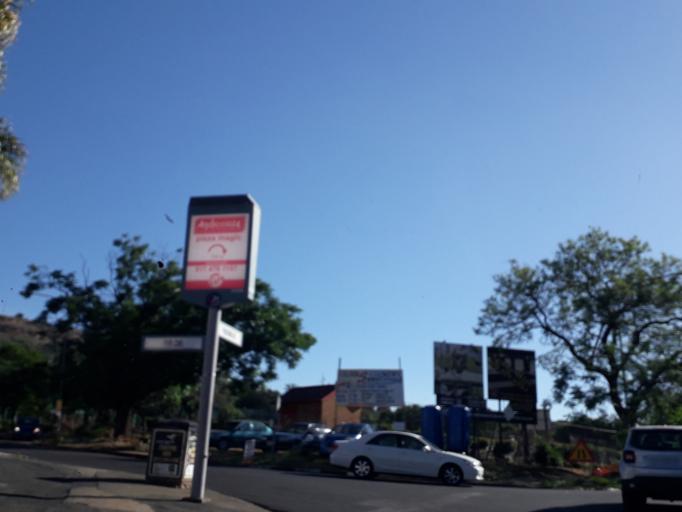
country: ZA
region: Gauteng
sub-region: City of Johannesburg Metropolitan Municipality
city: Roodepoort
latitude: -26.1339
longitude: 27.9654
